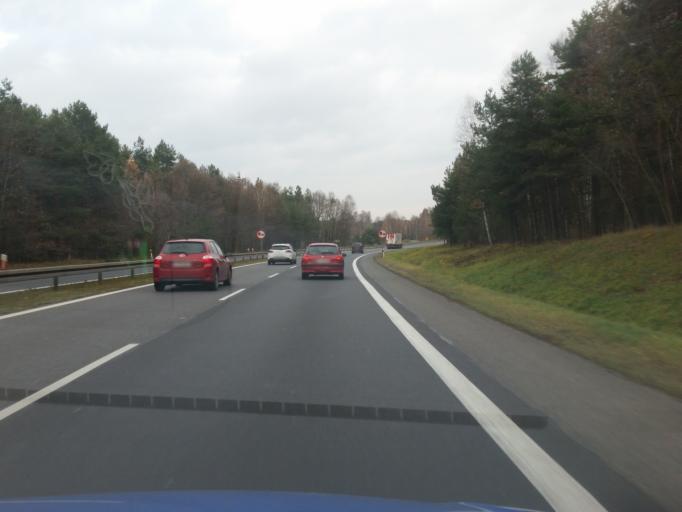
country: PL
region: Silesian Voivodeship
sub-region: Powiat czestochowski
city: Kamienica Polska
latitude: 50.6648
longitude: 19.1248
